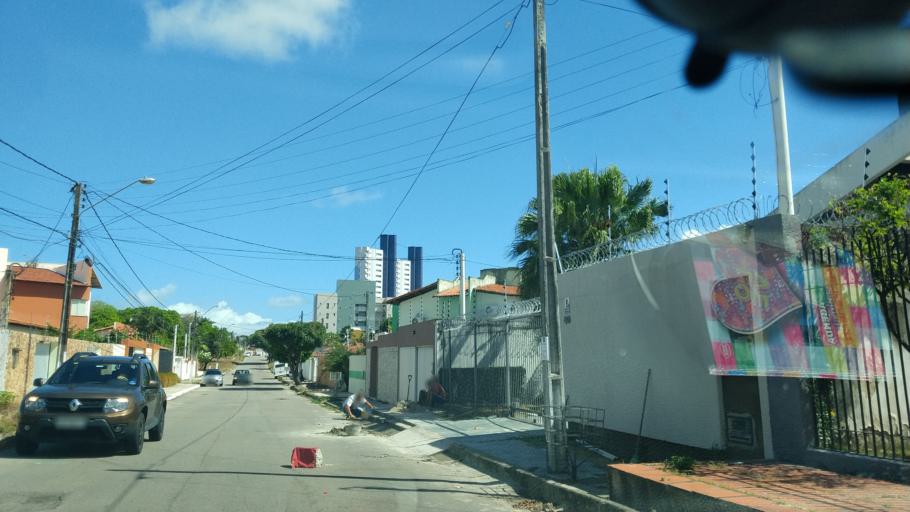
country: BR
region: Rio Grande do Norte
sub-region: Natal
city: Natal
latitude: -5.8696
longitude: -35.1927
